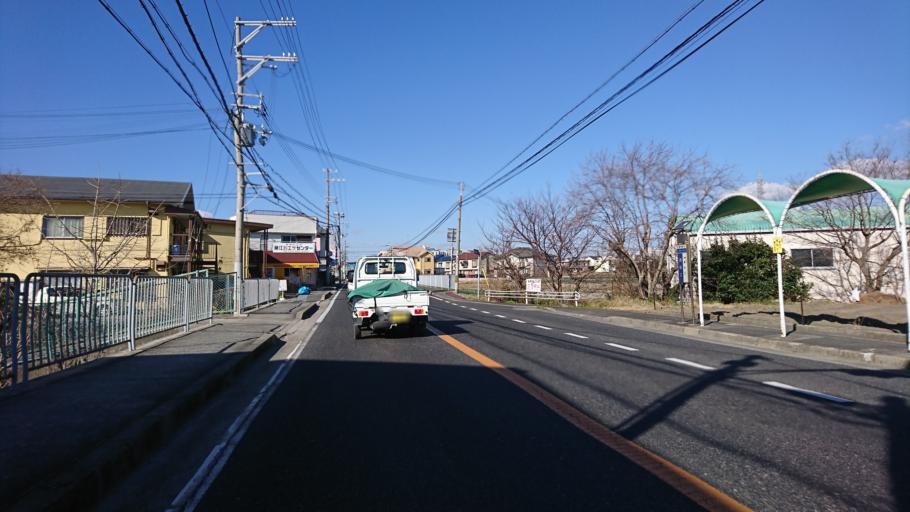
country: JP
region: Hyogo
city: Akashi
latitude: 34.6563
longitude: 134.9566
